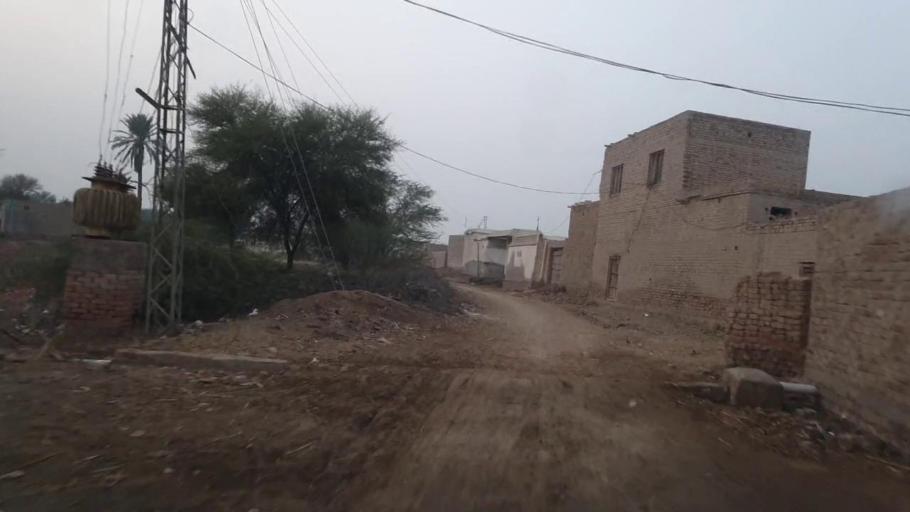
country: PK
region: Sindh
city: Karaundi
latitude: 26.9298
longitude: 68.4348
